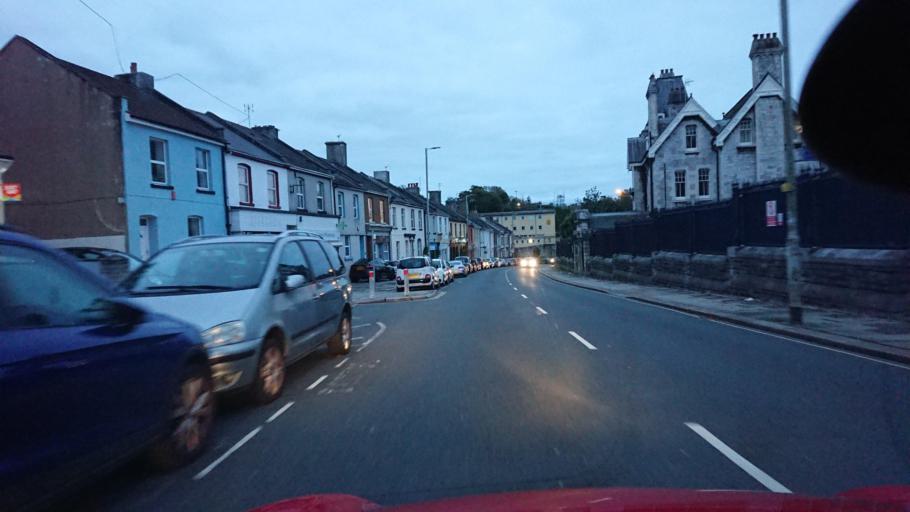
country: GB
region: England
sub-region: Cornwall
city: Torpoint
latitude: 50.3901
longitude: -4.1804
